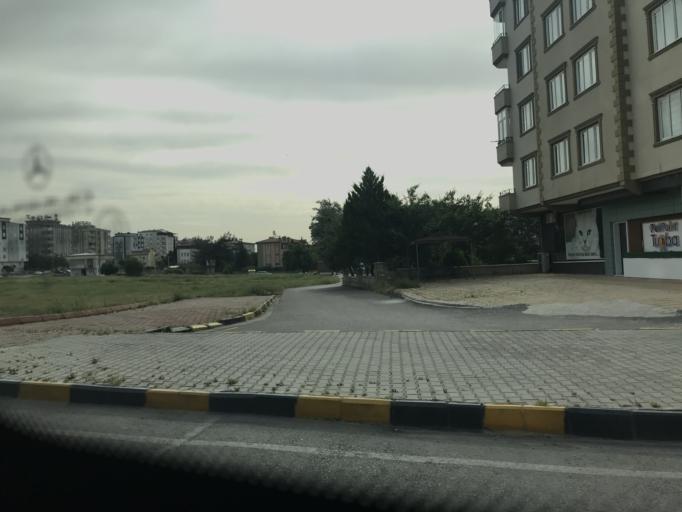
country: TR
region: Gaziantep
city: Sehitkamil
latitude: 37.0711
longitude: 37.3396
